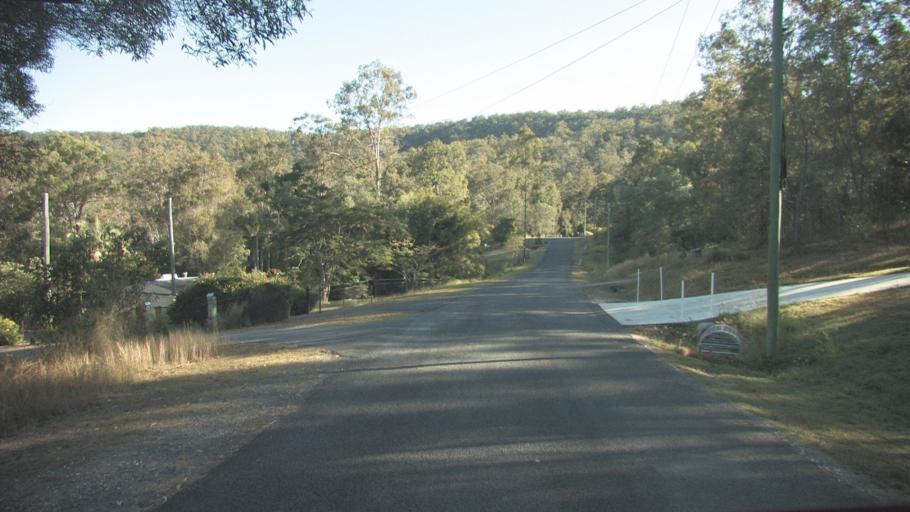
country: AU
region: Queensland
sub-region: Logan
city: Cedar Vale
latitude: -27.8354
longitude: 153.0922
